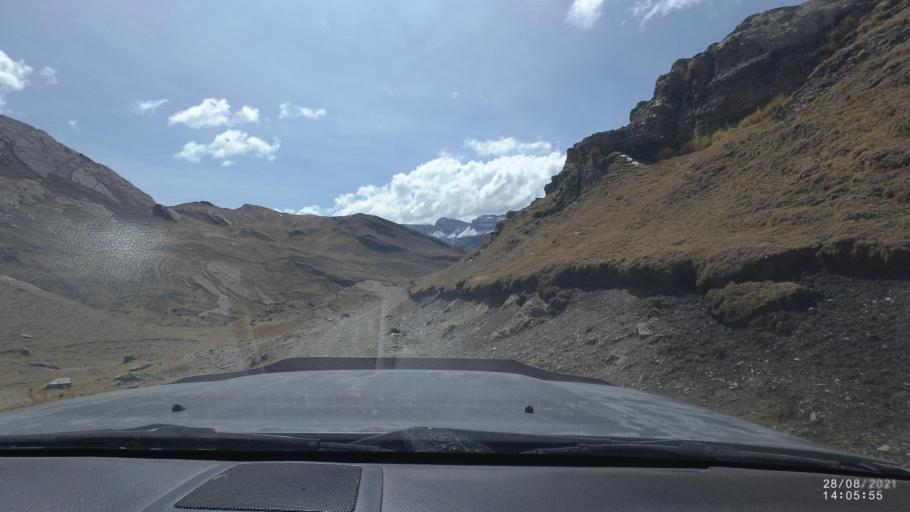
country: BO
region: Cochabamba
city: Sipe Sipe
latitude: -17.2705
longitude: -66.3832
